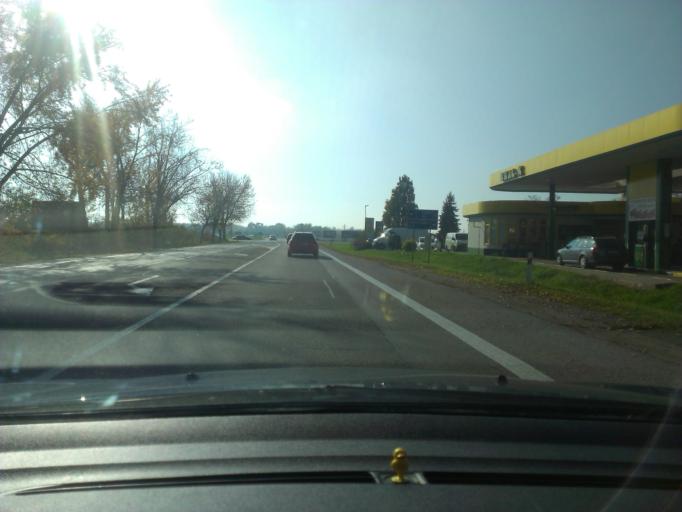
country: SK
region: Nitriansky
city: Komarno
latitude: 47.7684
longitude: 18.1540
